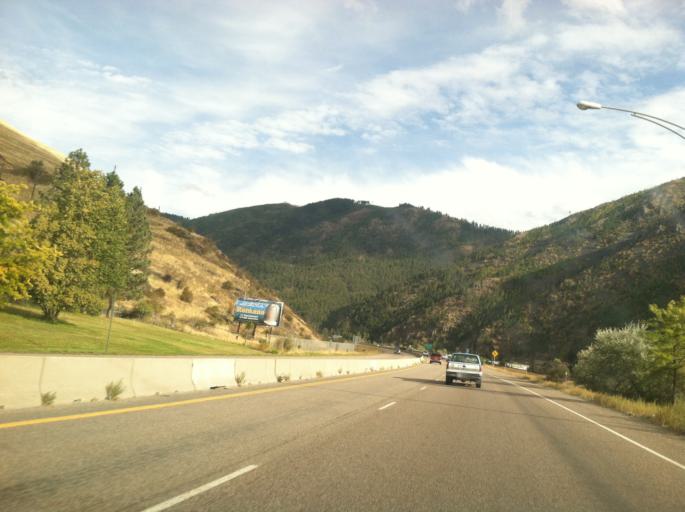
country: US
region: Montana
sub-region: Missoula County
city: Missoula
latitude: 46.8676
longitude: -113.9774
